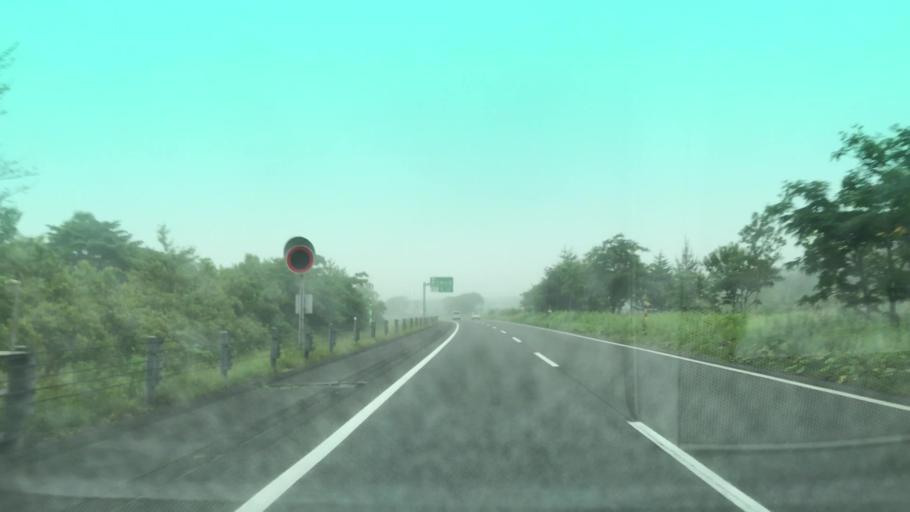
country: JP
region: Hokkaido
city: Chitose
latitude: 42.7810
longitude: 141.6269
